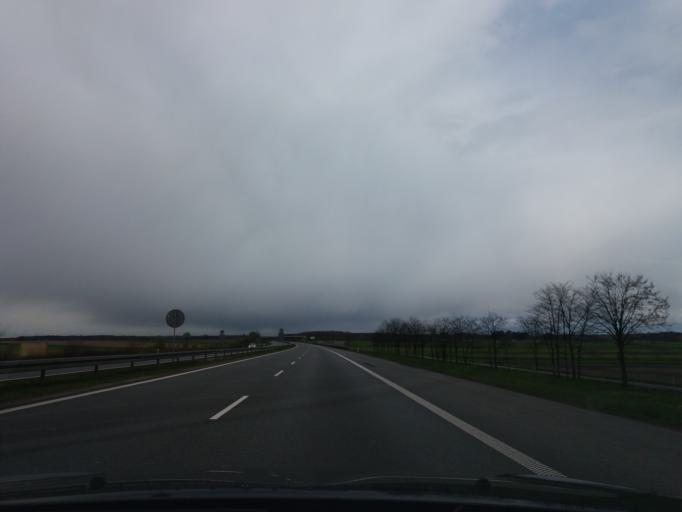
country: PL
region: Opole Voivodeship
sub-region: Powiat opolski
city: Proszkow
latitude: 50.5734
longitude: 17.8528
